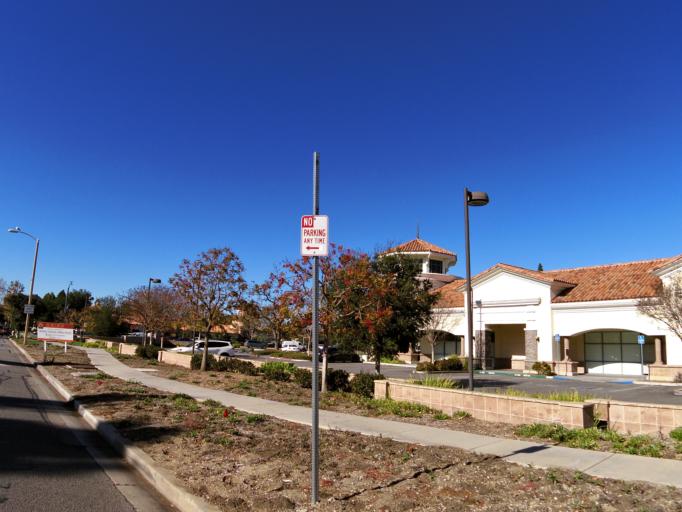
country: US
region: California
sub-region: Ventura County
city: Thousand Oaks
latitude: 34.1792
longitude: -118.8751
